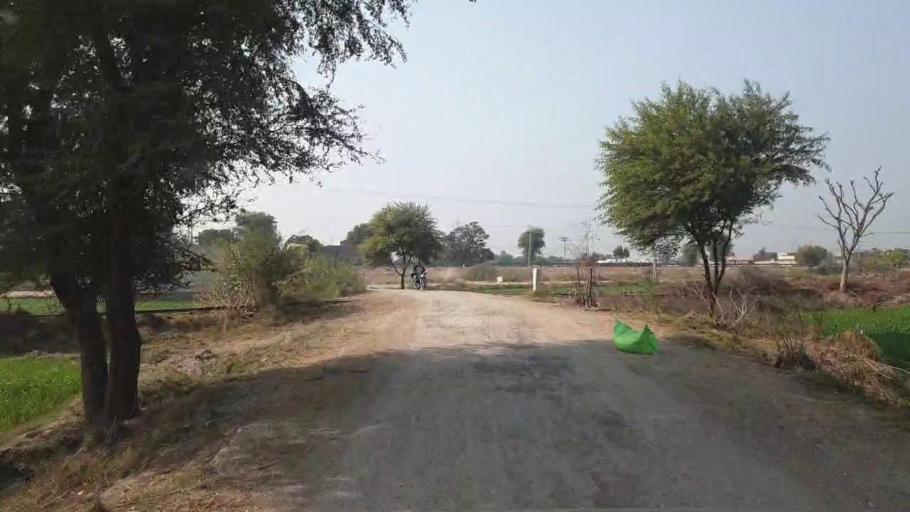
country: PK
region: Sindh
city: Hala
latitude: 25.8441
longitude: 68.4193
